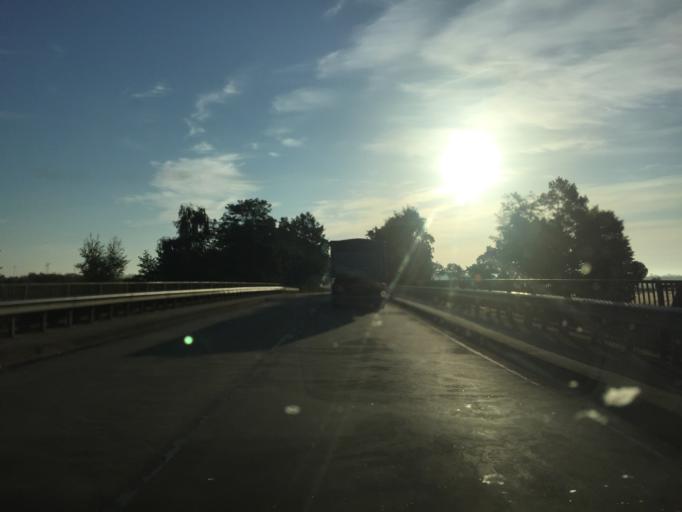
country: DE
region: Lower Saxony
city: Rethem
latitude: 52.7862
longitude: 9.3864
